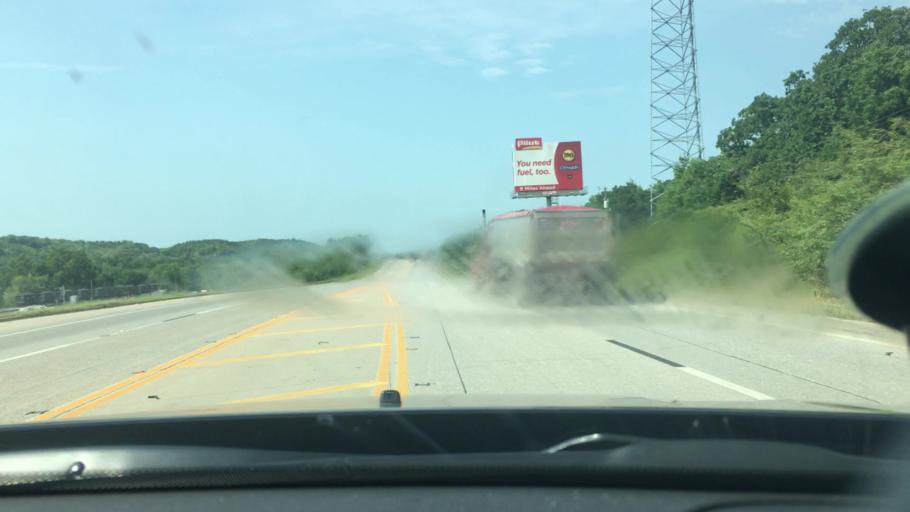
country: US
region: Oklahoma
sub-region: Atoka County
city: Atoka
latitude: 34.4725
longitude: -96.0531
